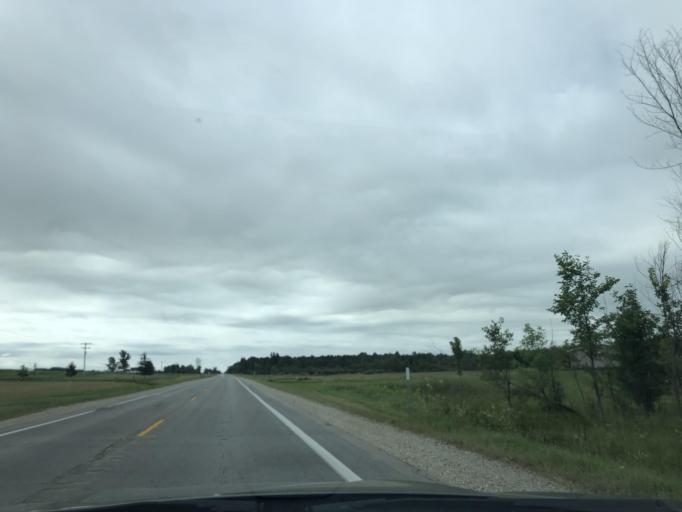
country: US
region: Michigan
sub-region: Missaukee County
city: Lake City
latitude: 44.2184
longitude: -85.2146
